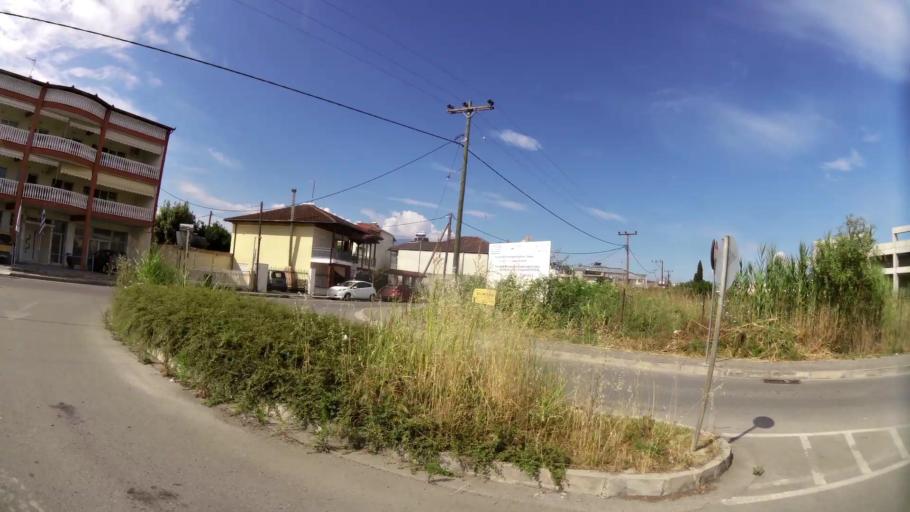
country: GR
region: Central Macedonia
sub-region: Nomos Pierias
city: Katerini
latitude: 40.2747
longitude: 22.5174
